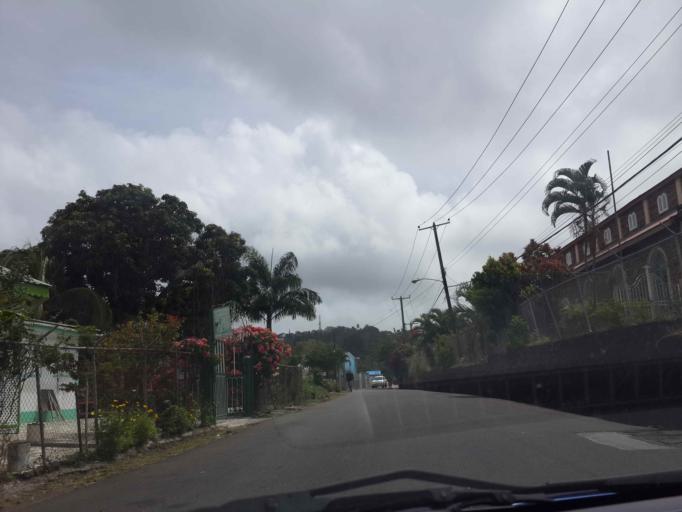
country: LC
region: Castries Quarter
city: Bisee
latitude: 14.0050
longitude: -60.9449
